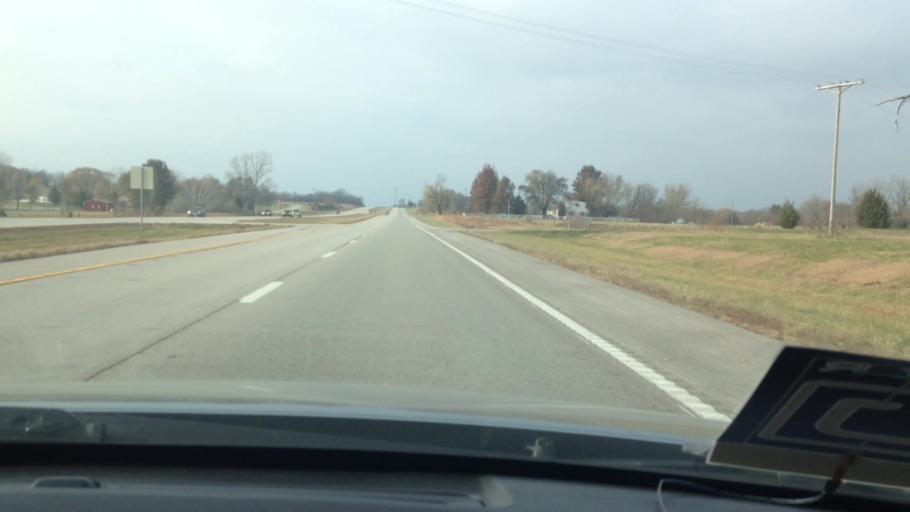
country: US
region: Missouri
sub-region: Cass County
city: Garden City
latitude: 38.5367
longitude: -94.1572
